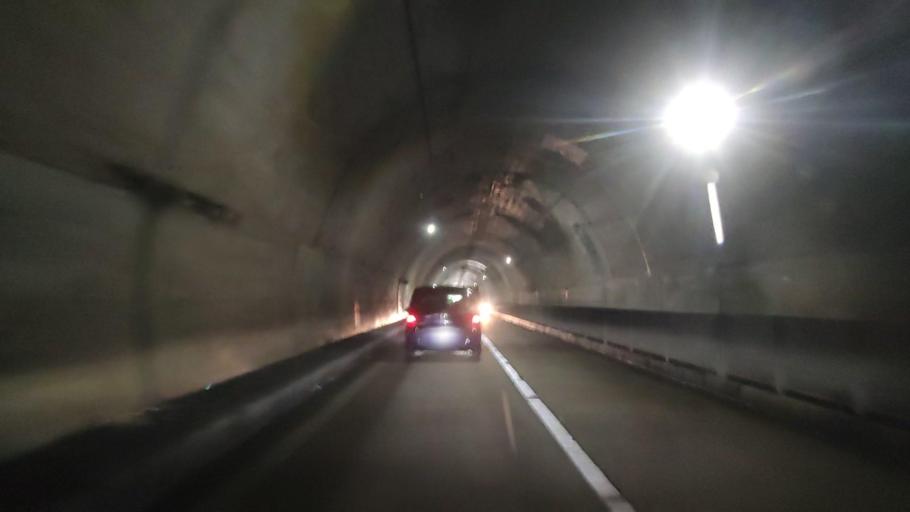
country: JP
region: Mie
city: Ise
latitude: 34.2706
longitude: 136.4899
